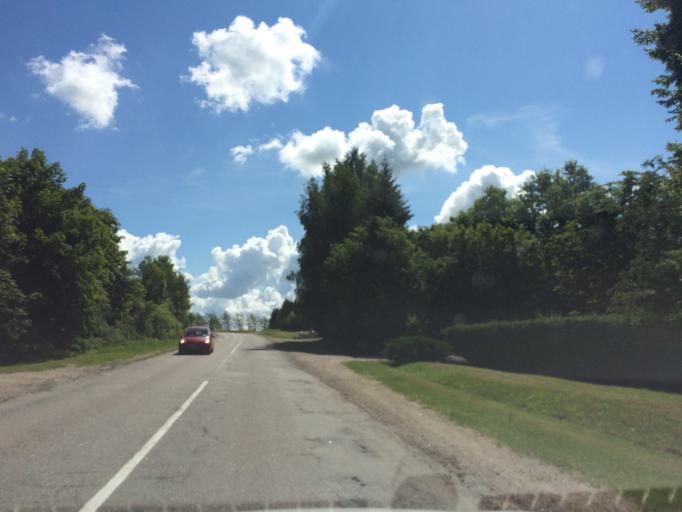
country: LV
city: Tervete
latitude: 56.4780
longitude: 23.3863
